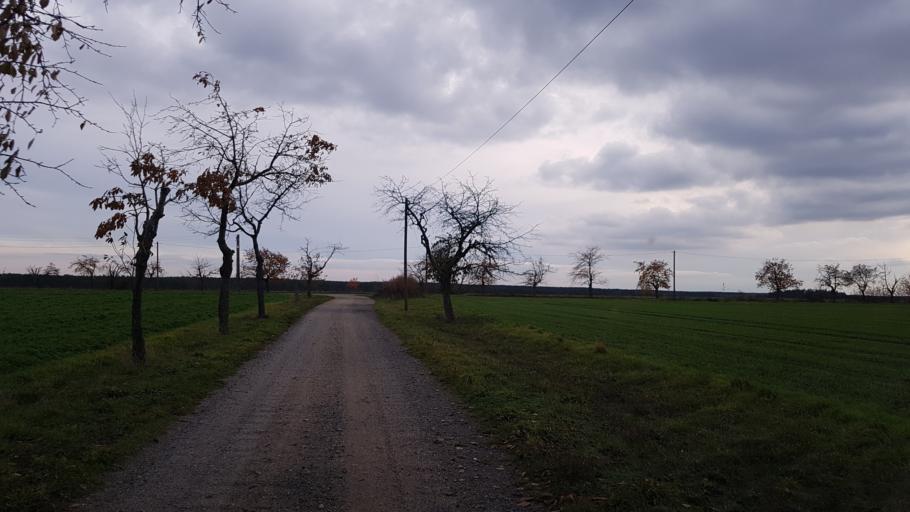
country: DE
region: Brandenburg
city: Trobitz
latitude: 51.6624
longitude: 13.4211
